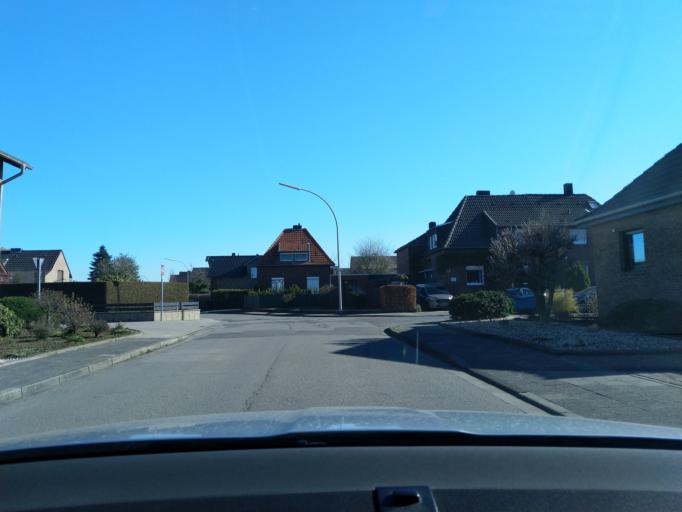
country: DE
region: North Rhine-Westphalia
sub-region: Regierungsbezirk Dusseldorf
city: Monchengladbach
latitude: 51.1150
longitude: 6.4171
